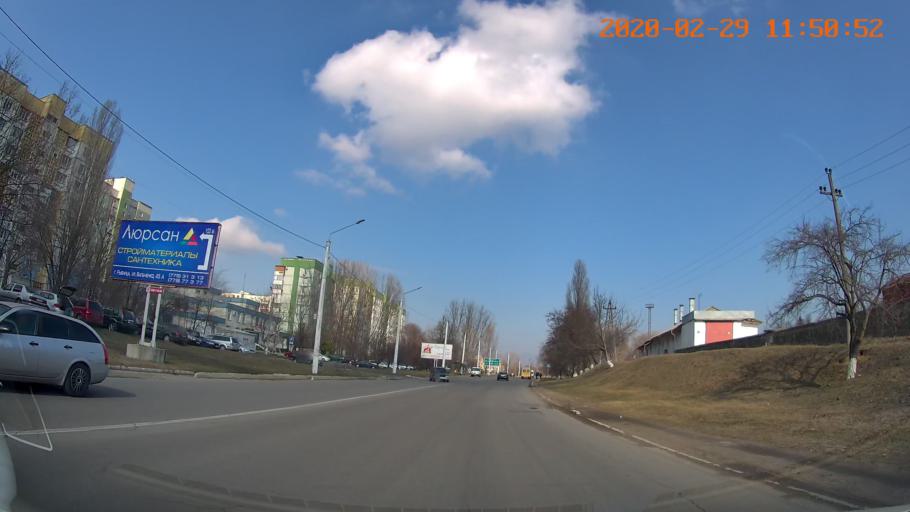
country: MD
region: Telenesti
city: Ribnita
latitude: 47.7617
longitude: 28.9896
